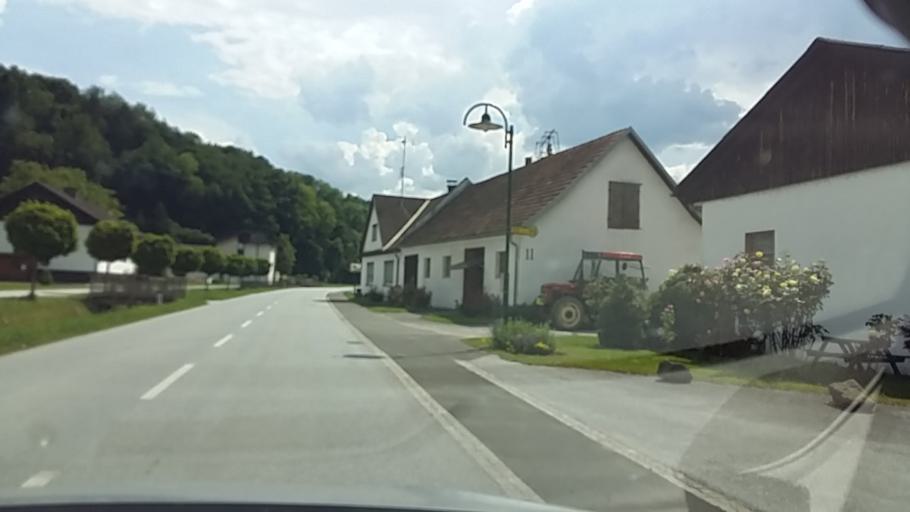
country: AT
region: Styria
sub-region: Politischer Bezirk Suedoststeiermark
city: Breitenfeld an der Rittschein
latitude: 47.0329
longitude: 15.9599
